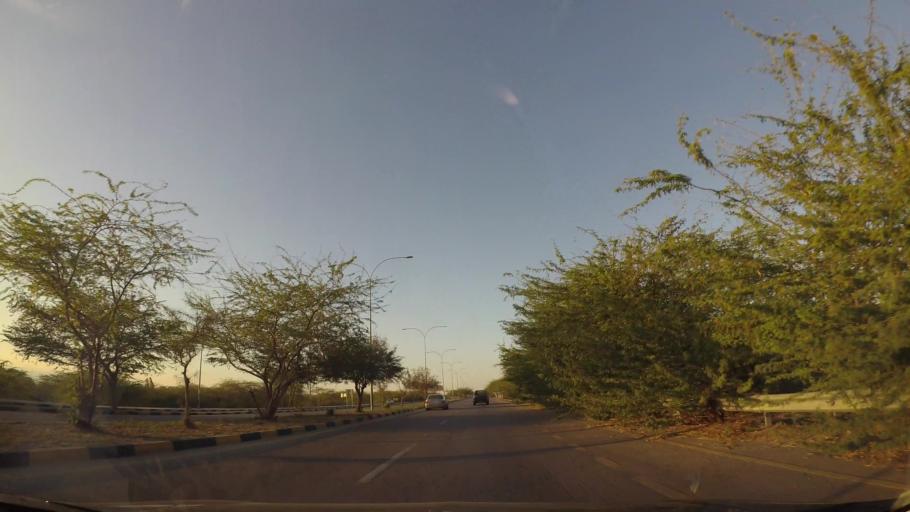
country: PS
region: West Bank
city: Jericho
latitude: 31.7728
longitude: 35.5925
